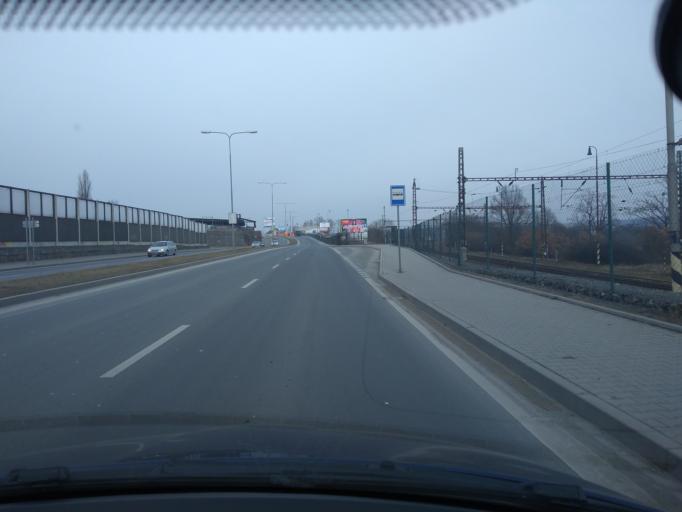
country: CZ
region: Plzensky
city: Stenovice
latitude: 49.7157
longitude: 13.4172
